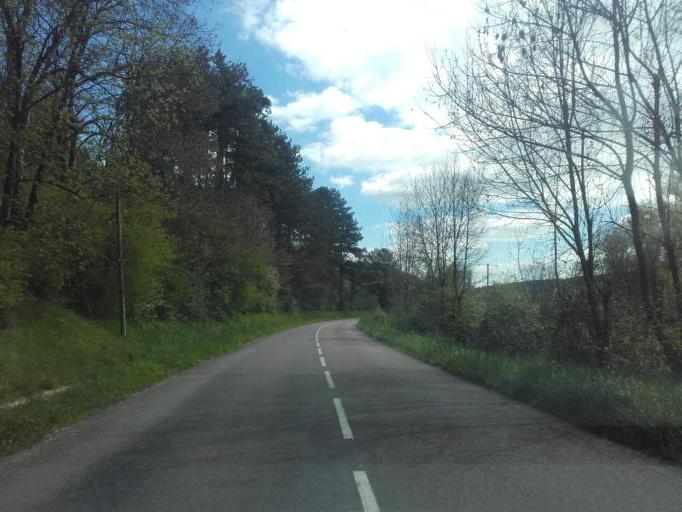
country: FR
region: Bourgogne
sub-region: Departement de la Cote-d'Or
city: Meursault
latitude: 47.0191
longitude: 4.7591
